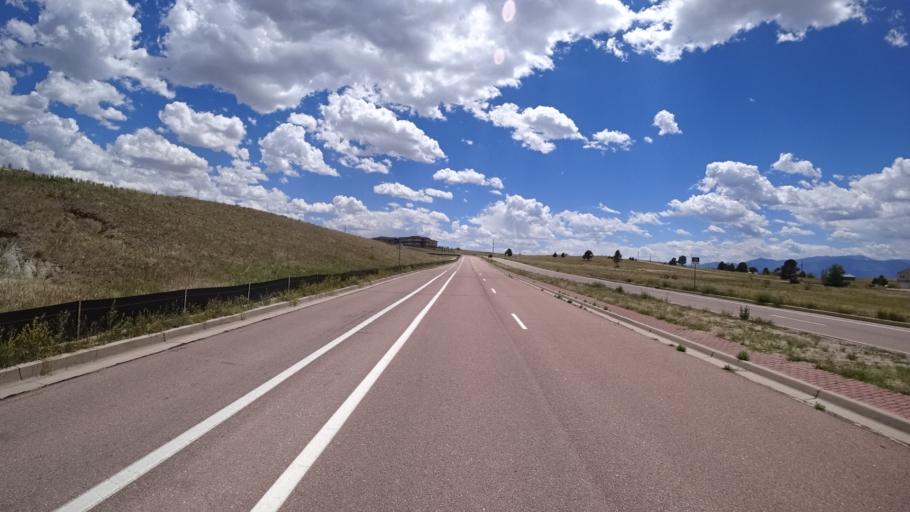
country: US
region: Colorado
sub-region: El Paso County
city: Black Forest
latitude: 38.9460
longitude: -104.7147
